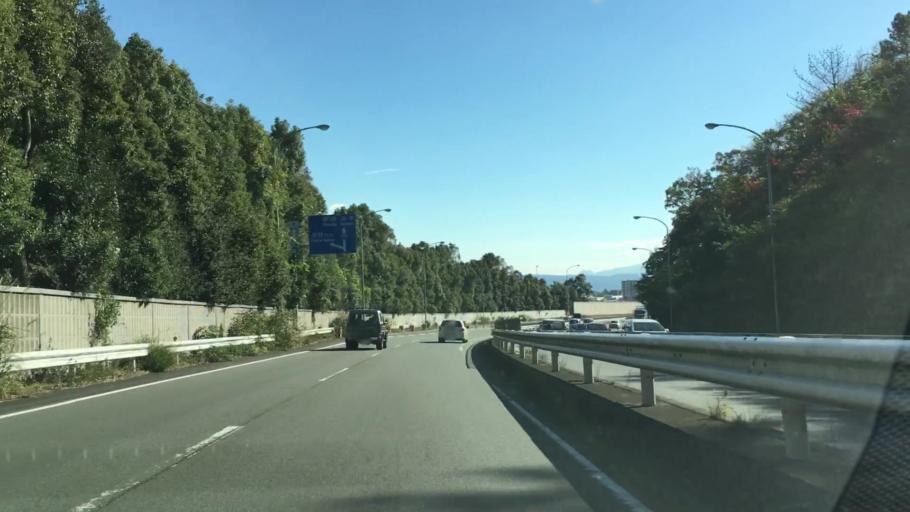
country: JP
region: Shizuoka
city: Mishima
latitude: 35.1731
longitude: 138.9006
